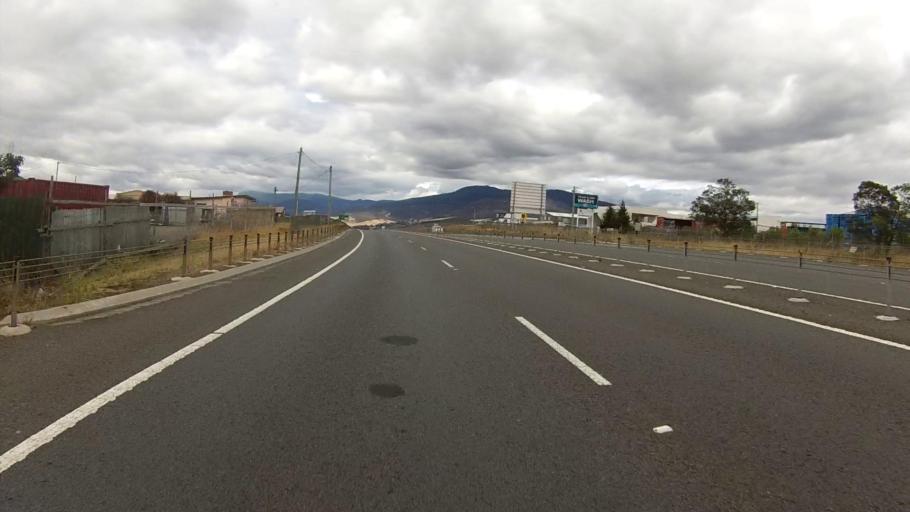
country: AU
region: Tasmania
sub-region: Brighton
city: Bridgewater
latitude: -42.7188
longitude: 147.2384
